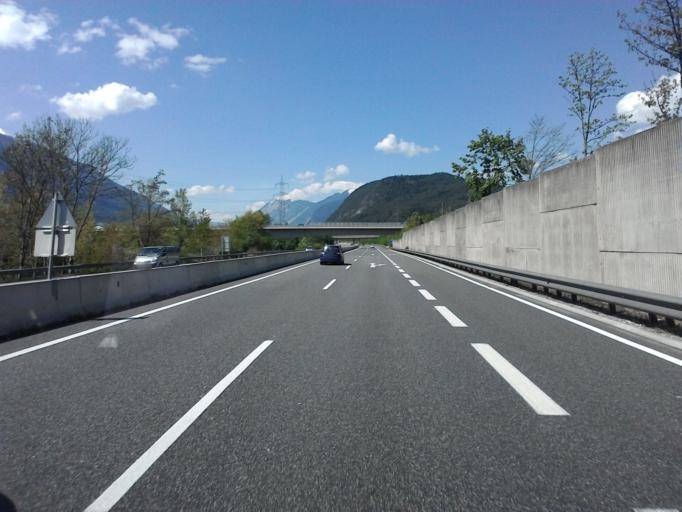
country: AT
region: Tyrol
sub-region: Politischer Bezirk Innsbruck Land
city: Telfs
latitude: 47.3022
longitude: 11.0737
